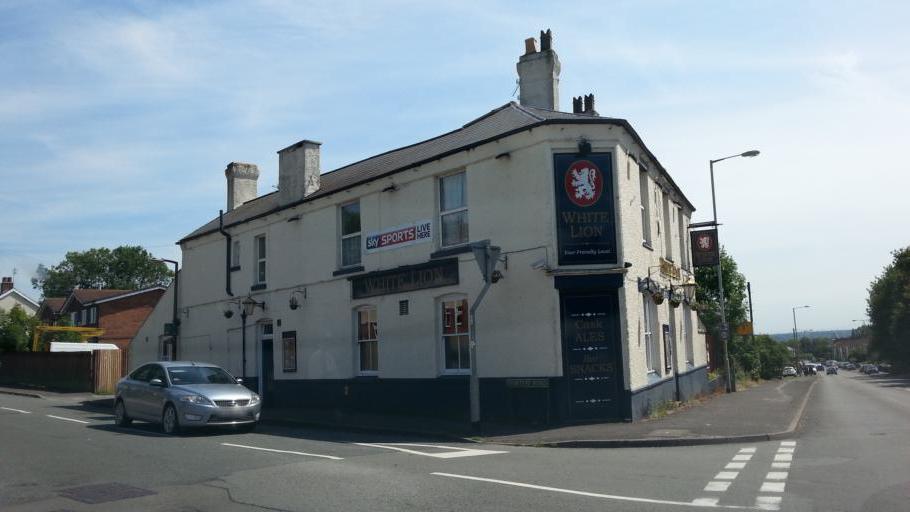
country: GB
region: England
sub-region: Staffordshire
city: Cannock
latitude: 52.7023
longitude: -2.0368
